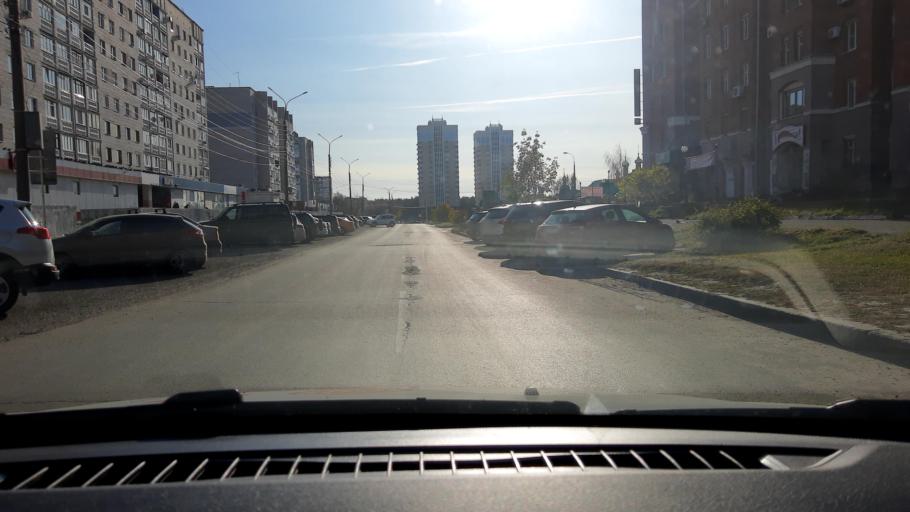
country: RU
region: Nizjnij Novgorod
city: Dzerzhinsk
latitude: 56.2312
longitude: 43.4161
